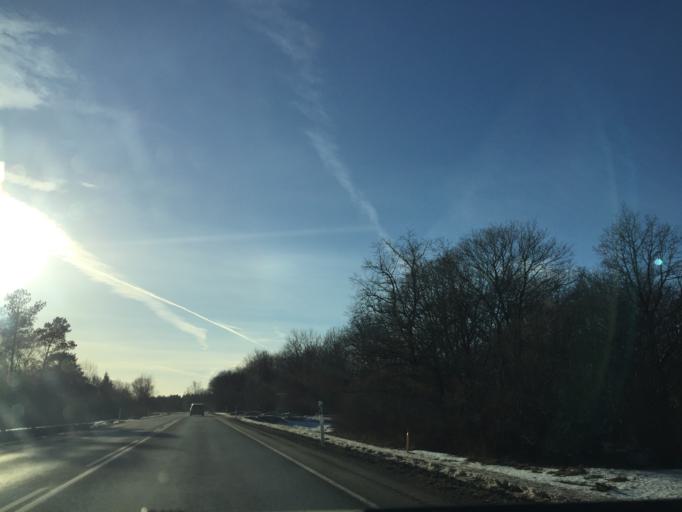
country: EE
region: Saare
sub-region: Kuressaare linn
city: Kuressaare
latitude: 58.2931
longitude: 22.5659
